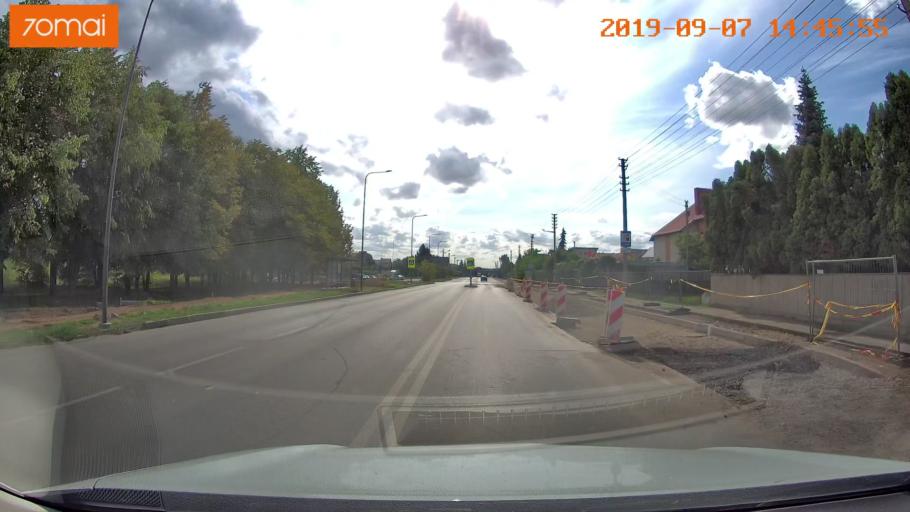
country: LT
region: Kauno apskritis
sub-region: Kaunas
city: Silainiai
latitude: 54.9296
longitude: 23.9076
